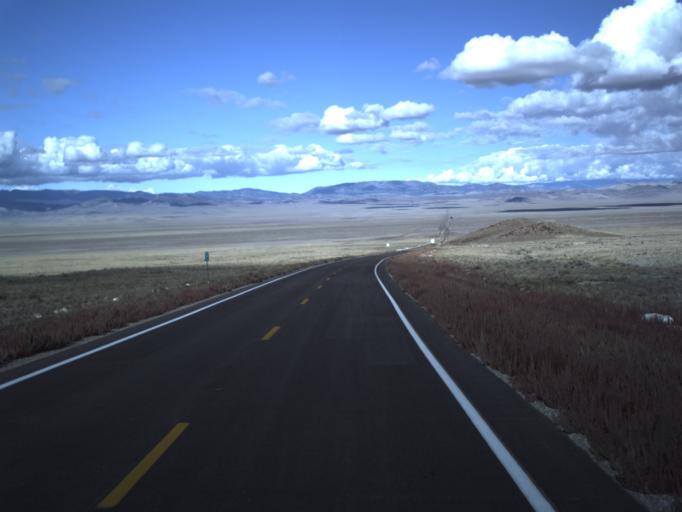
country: US
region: Utah
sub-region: Beaver County
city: Milford
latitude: 38.5065
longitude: -113.6114
